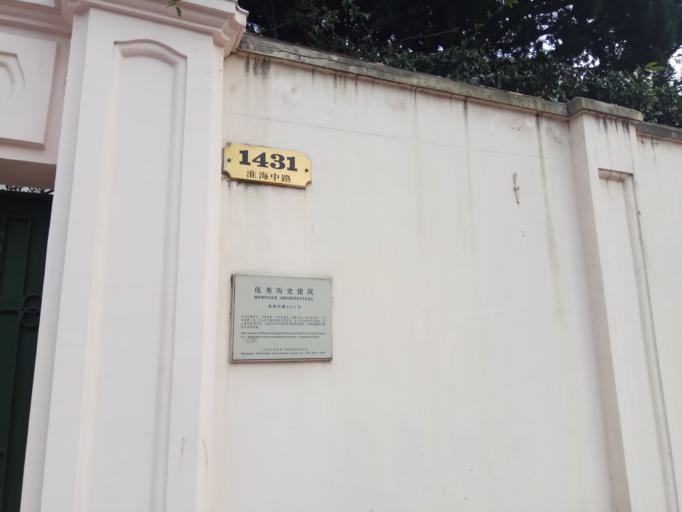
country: CN
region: Shanghai Shi
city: Xuhui
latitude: 31.2118
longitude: 121.4428
